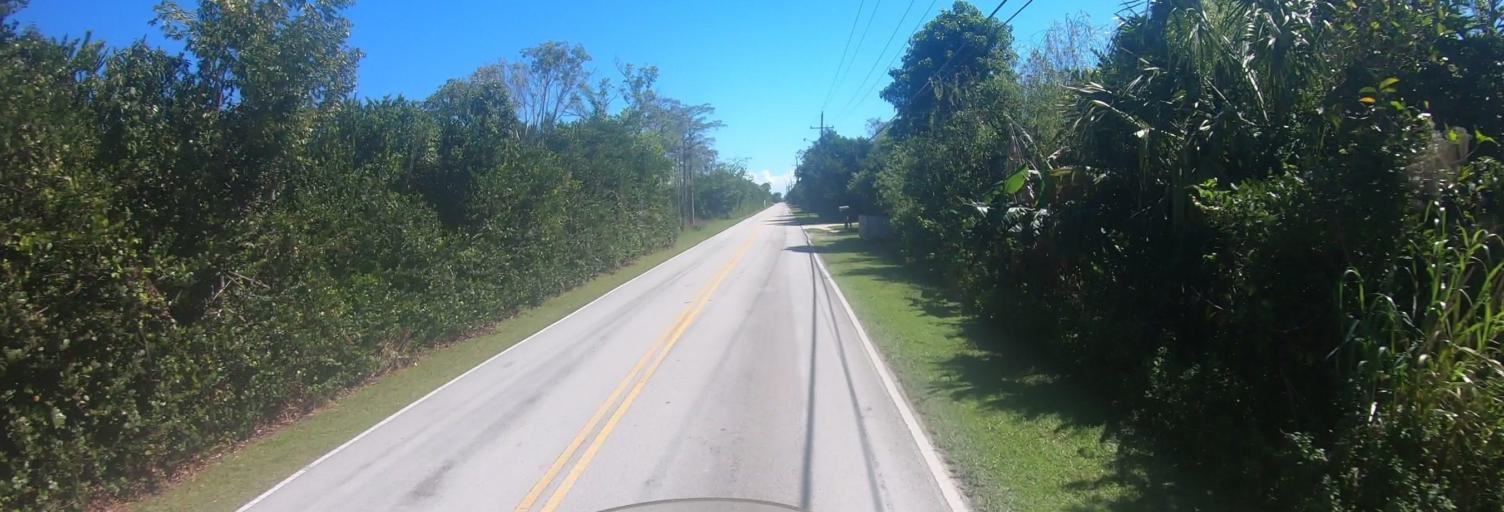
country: US
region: Florida
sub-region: Miami-Dade County
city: Kendall West
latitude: 25.7607
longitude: -80.8333
